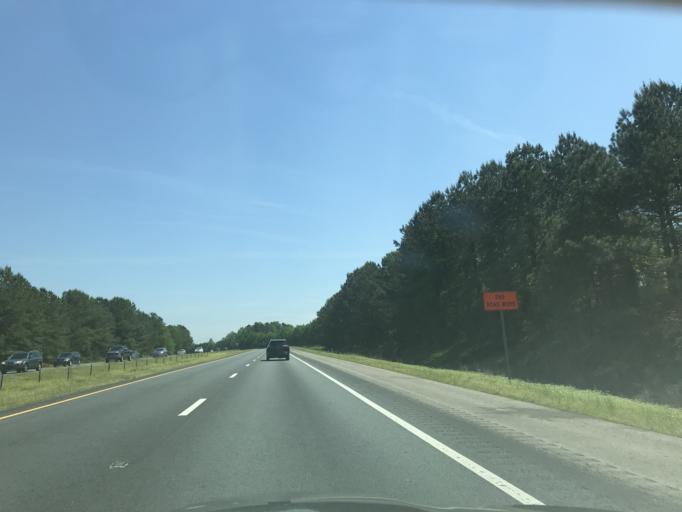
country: US
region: North Carolina
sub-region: Johnston County
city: Benson
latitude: 35.3749
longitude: -78.5033
